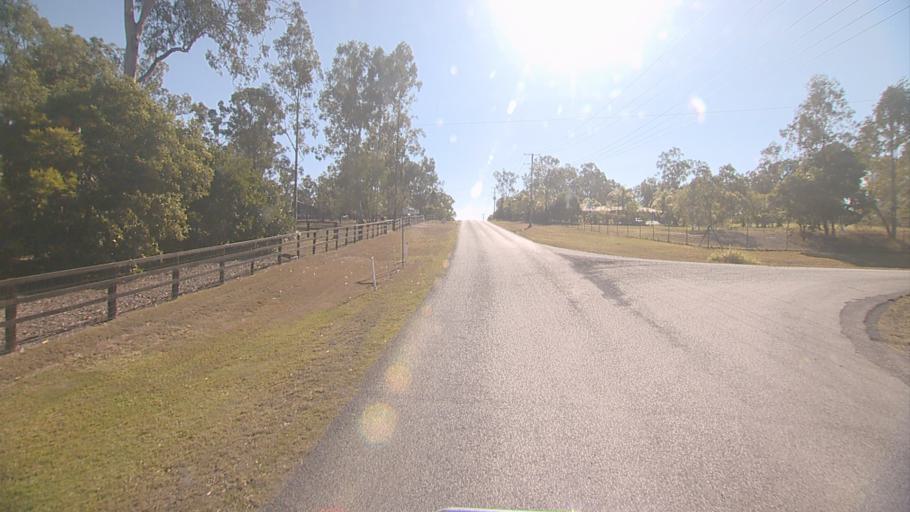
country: AU
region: Queensland
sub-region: Logan
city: Cedar Vale
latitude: -27.8290
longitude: 153.0445
